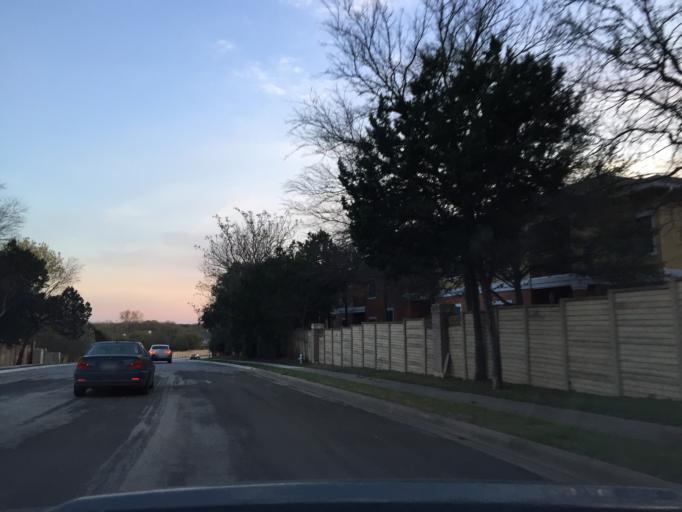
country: US
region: Texas
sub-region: Travis County
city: Wells Branch
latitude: 30.4289
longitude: -97.6956
